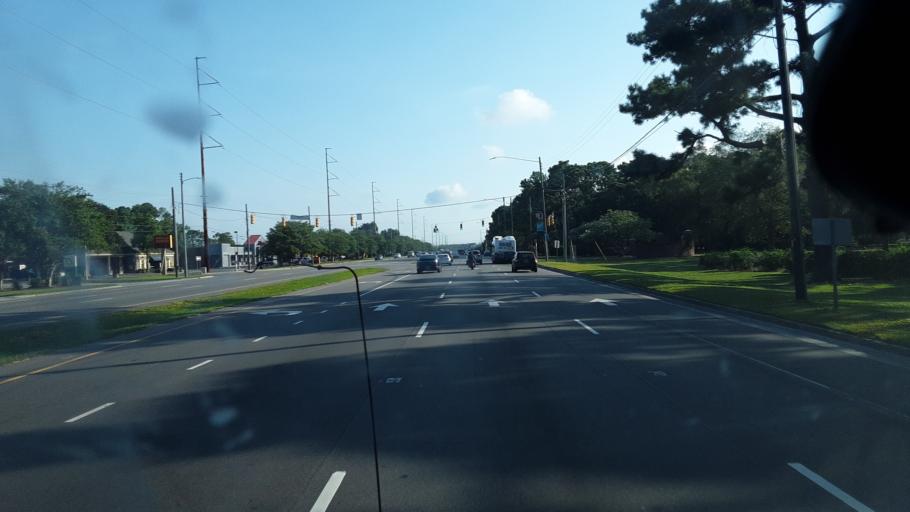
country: US
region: North Carolina
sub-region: New Hanover County
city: Seagate
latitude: 34.2262
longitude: -77.8799
